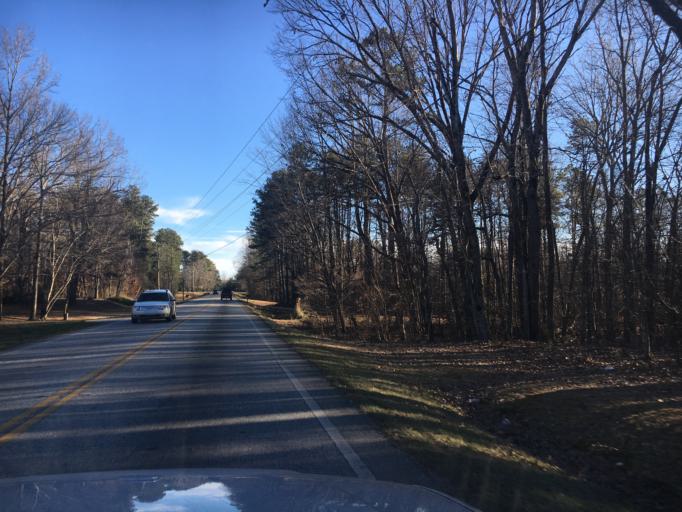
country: US
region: Georgia
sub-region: Habersham County
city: Demorest
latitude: 34.5575
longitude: -83.5746
